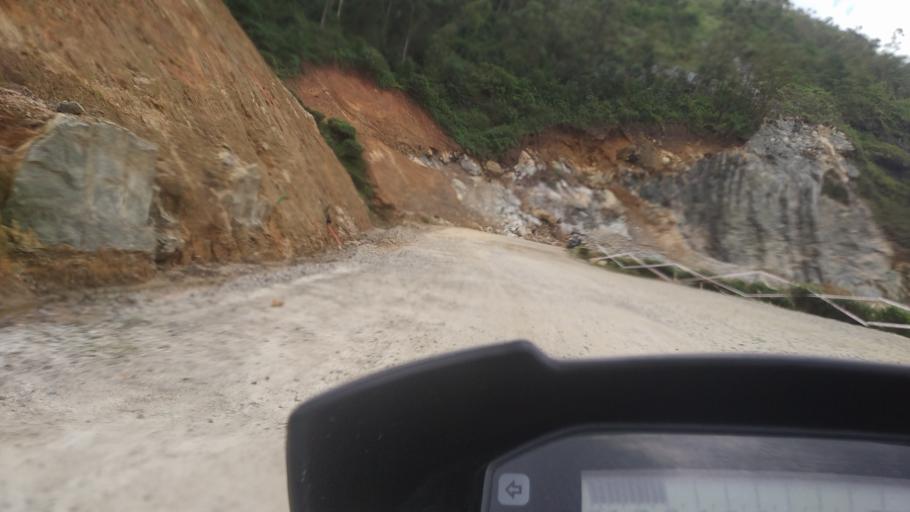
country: IN
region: Kerala
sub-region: Idukki
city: Munnar
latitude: 10.0376
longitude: 77.1529
